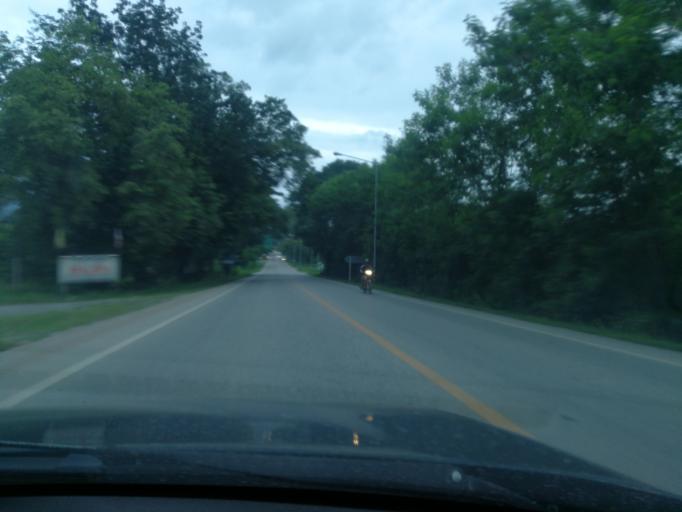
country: TH
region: Chiang Mai
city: Hot
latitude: 18.1840
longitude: 98.6181
